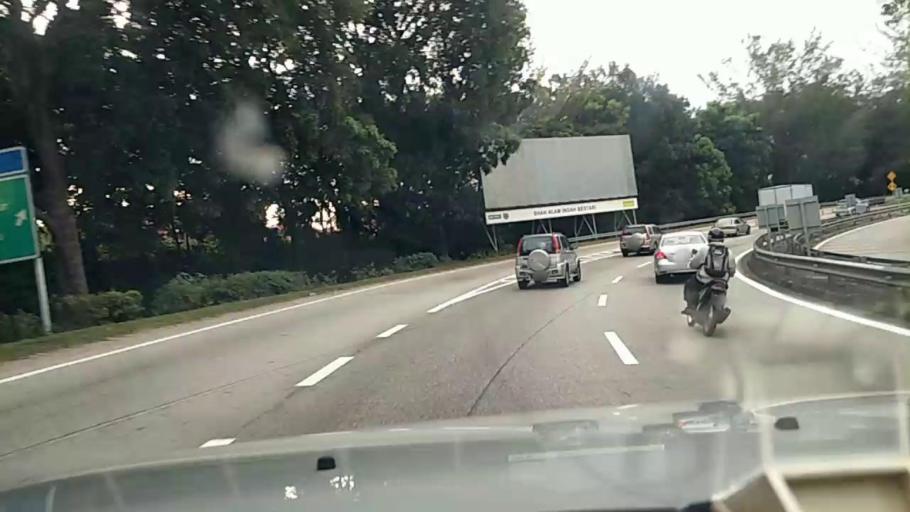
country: MY
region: Selangor
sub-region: Petaling
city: Petaling Jaya
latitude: 3.0990
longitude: 101.5876
